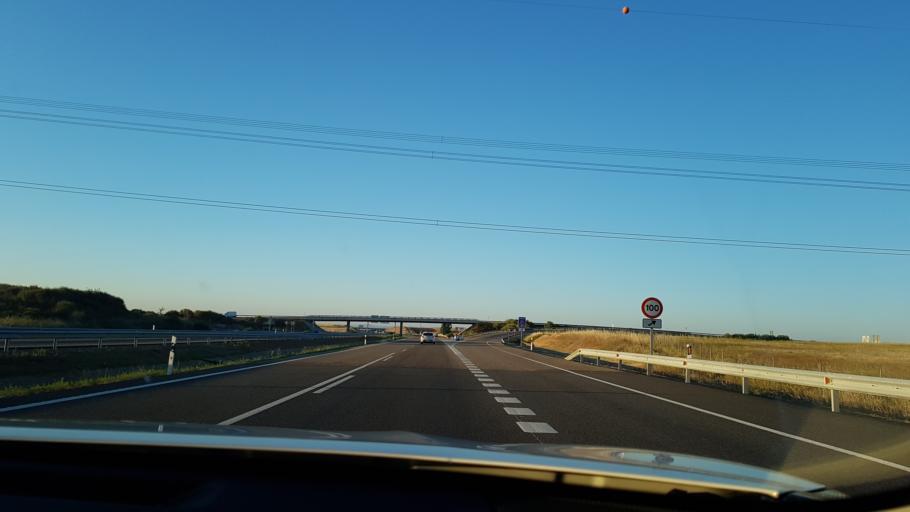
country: ES
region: Castille and Leon
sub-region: Provincia de Zamora
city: Roales
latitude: 41.5805
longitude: -5.7759
